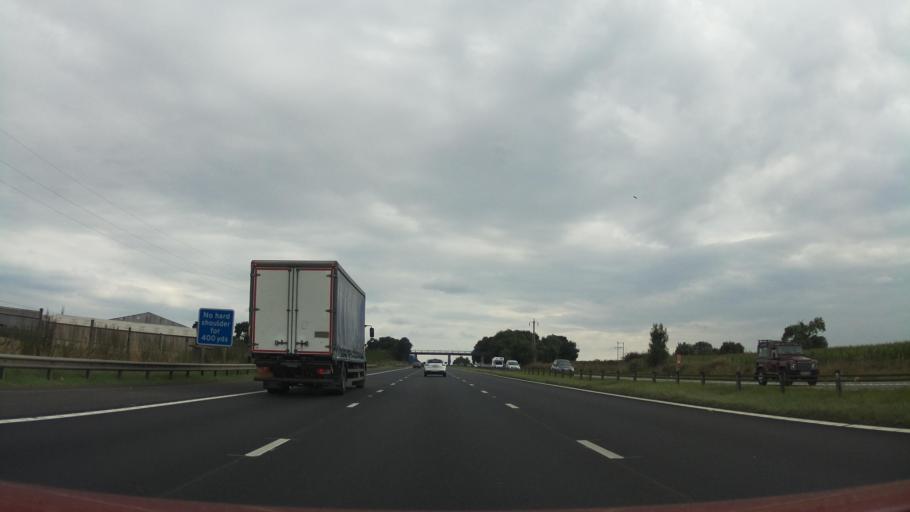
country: GB
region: England
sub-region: County Durham
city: Coxhoe
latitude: 54.7569
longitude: -1.5249
